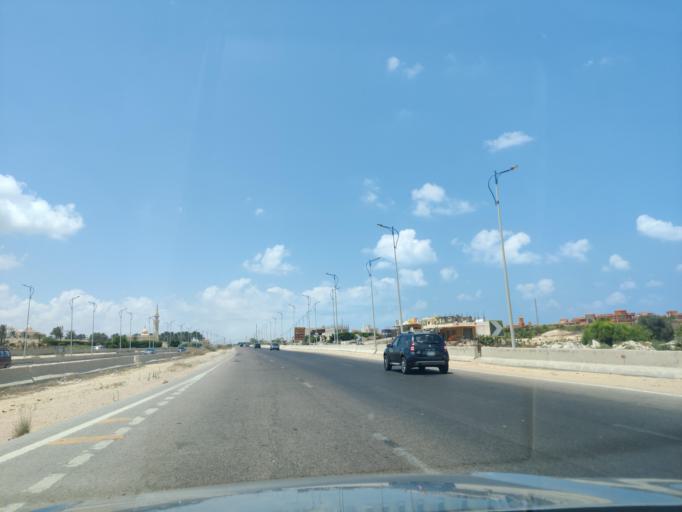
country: EG
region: Alexandria
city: Alexandria
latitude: 30.9883
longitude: 29.5906
